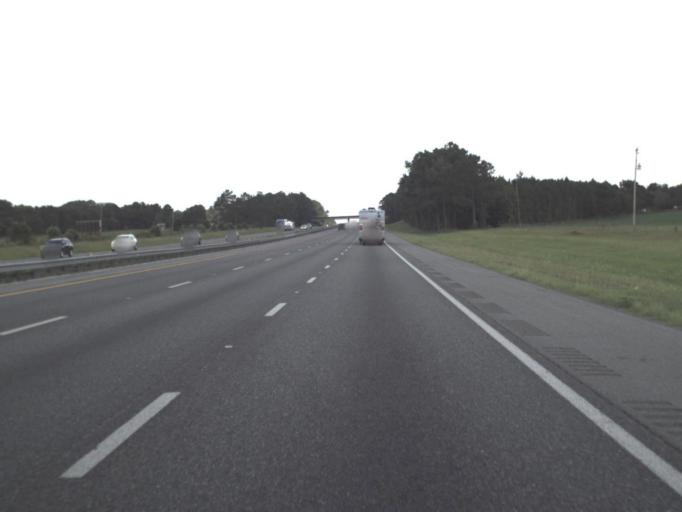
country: US
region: Florida
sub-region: Columbia County
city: Lake City
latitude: 30.0637
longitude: -82.6266
